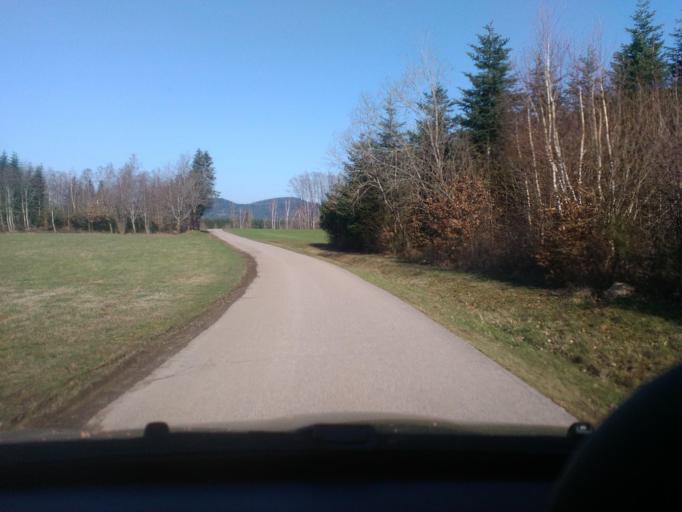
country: FR
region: Lorraine
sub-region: Departement des Vosges
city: Moyenmoutier
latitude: 48.3639
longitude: 6.9173
